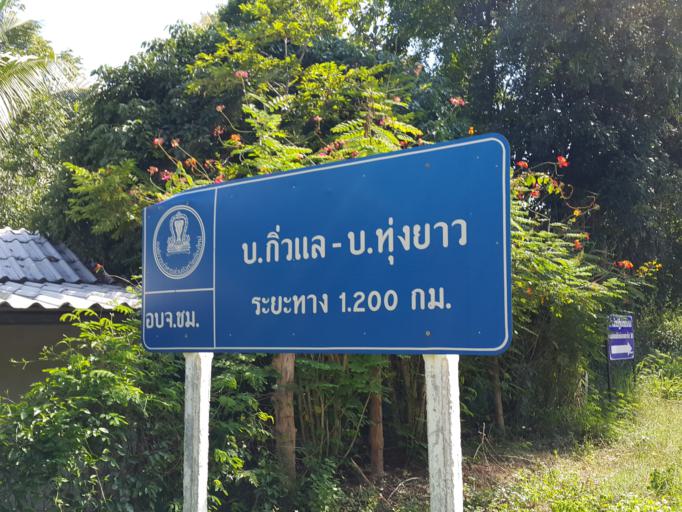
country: TH
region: Chiang Mai
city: San Sai
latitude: 18.8659
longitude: 99.1578
